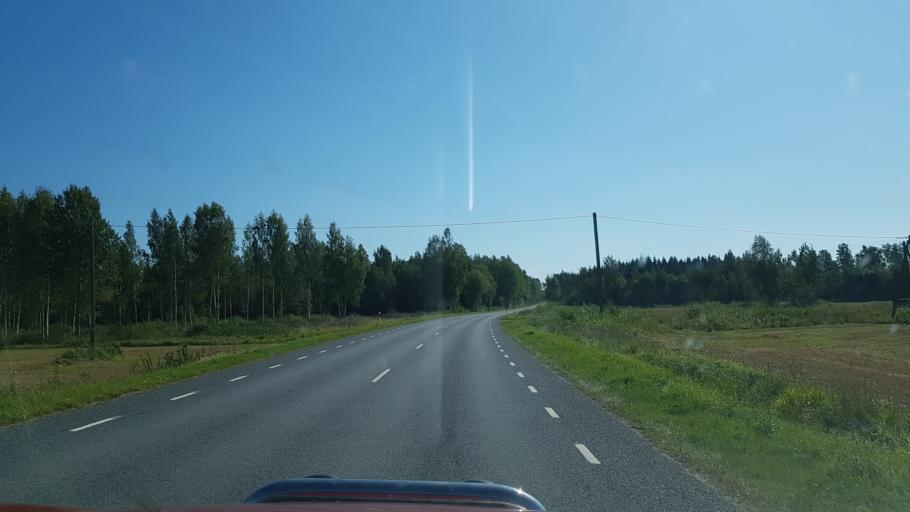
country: EE
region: Polvamaa
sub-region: Polva linn
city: Polva
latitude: 58.2763
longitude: 27.1115
